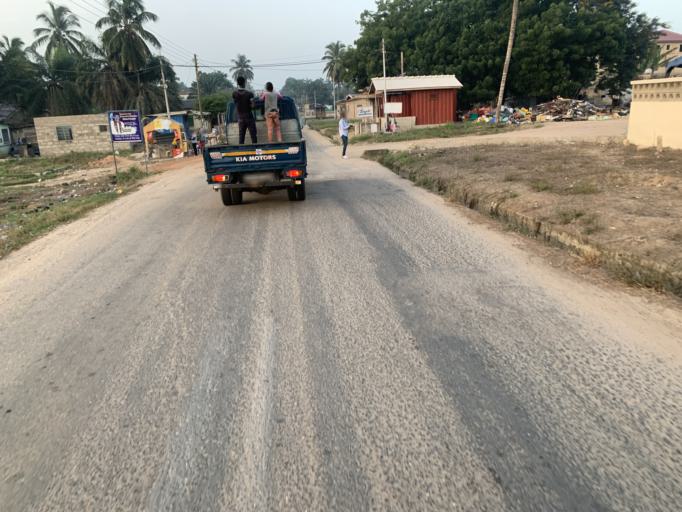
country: GH
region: Central
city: Winneba
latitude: 5.3509
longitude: -0.6276
